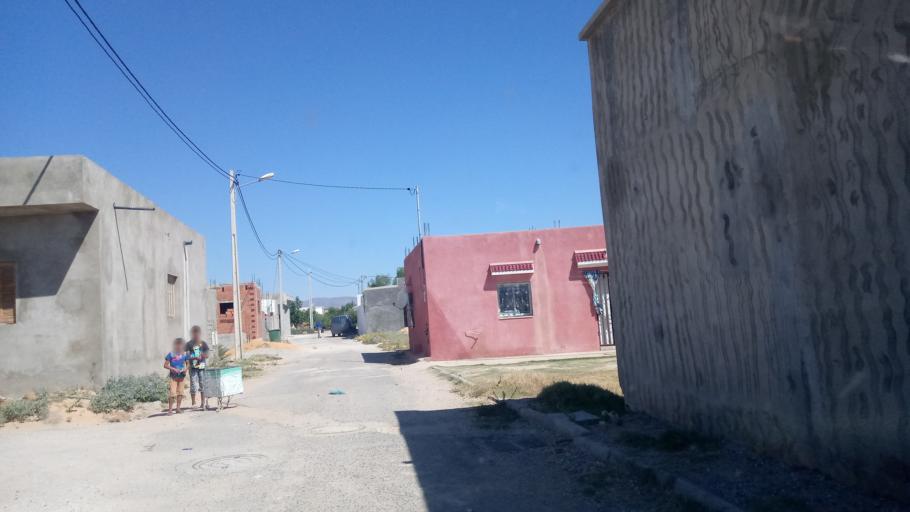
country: TN
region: Al Qayrawan
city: Sbikha
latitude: 36.1290
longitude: 10.0905
